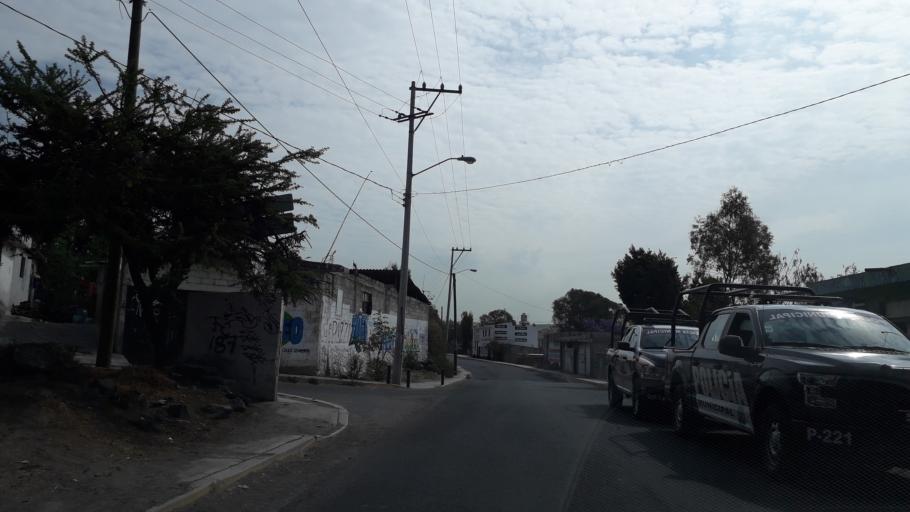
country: MX
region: Puebla
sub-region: Puebla
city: San Andres Azumiatla
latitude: 18.9075
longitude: -98.2444
